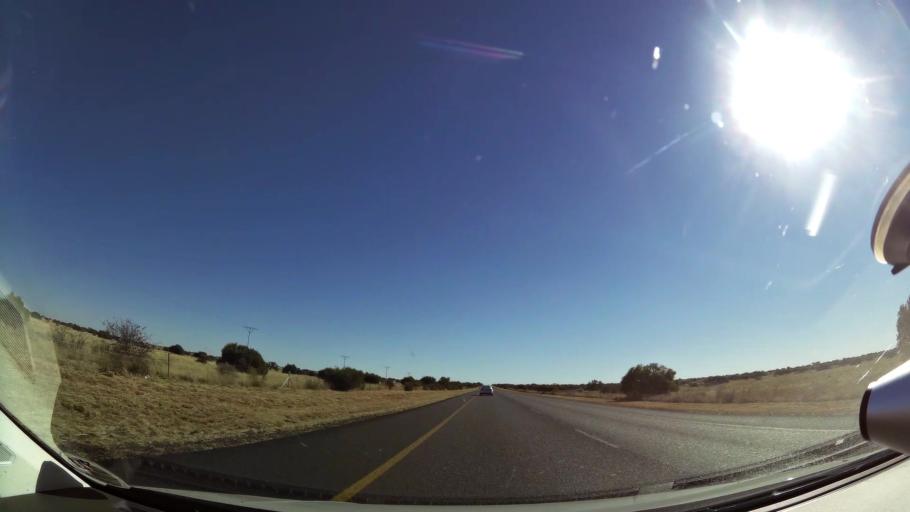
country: ZA
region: Northern Cape
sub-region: Frances Baard District Municipality
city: Warrenton
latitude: -28.2179
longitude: 24.8480
